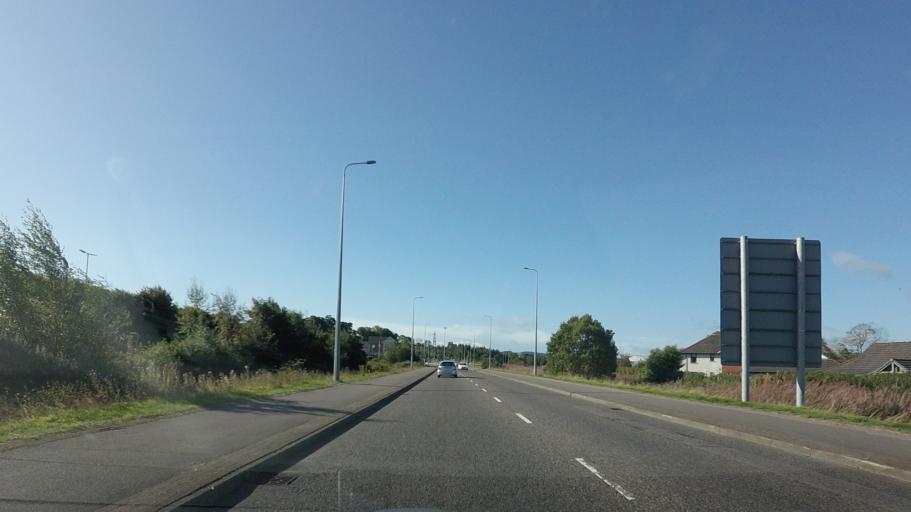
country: GB
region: Scotland
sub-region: Highland
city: Inverness
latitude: 57.4520
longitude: -4.2165
